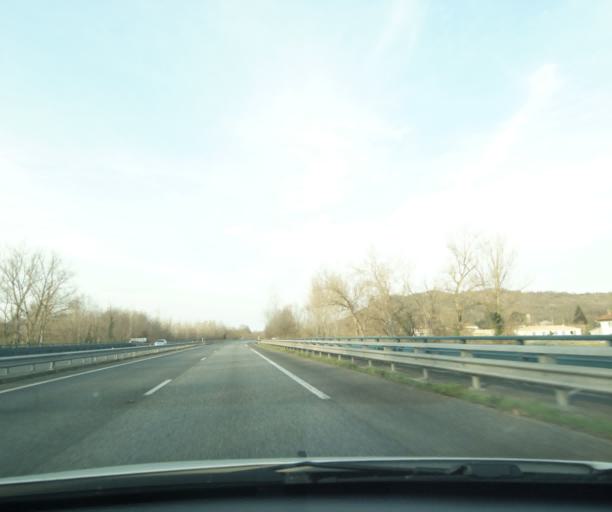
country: FR
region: Midi-Pyrenees
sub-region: Departement de la Haute-Garonne
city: Salies-du-Salat
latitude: 43.1587
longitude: 0.9670
